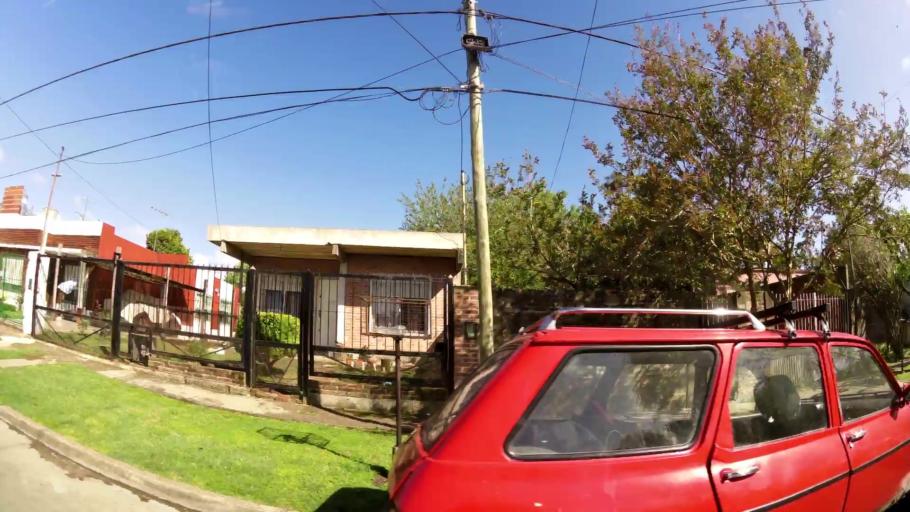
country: AR
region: Buenos Aires
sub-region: Partido de Quilmes
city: Quilmes
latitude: -34.7919
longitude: -58.1455
